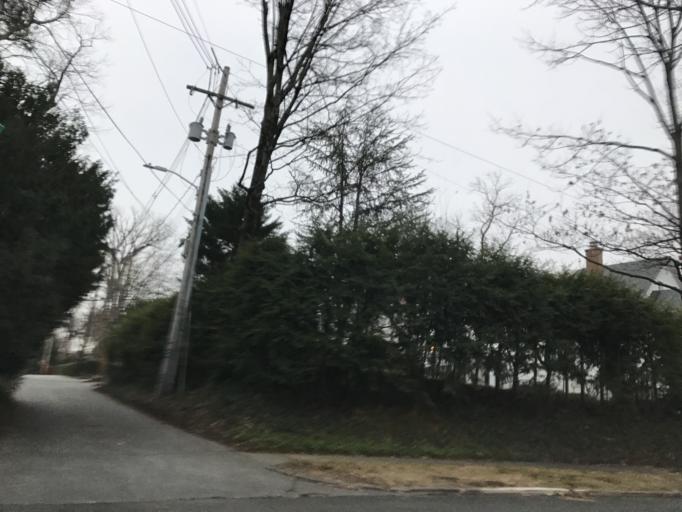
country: US
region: Maryland
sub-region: City of Baltimore
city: Baltimore
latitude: 39.3458
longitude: -76.6373
